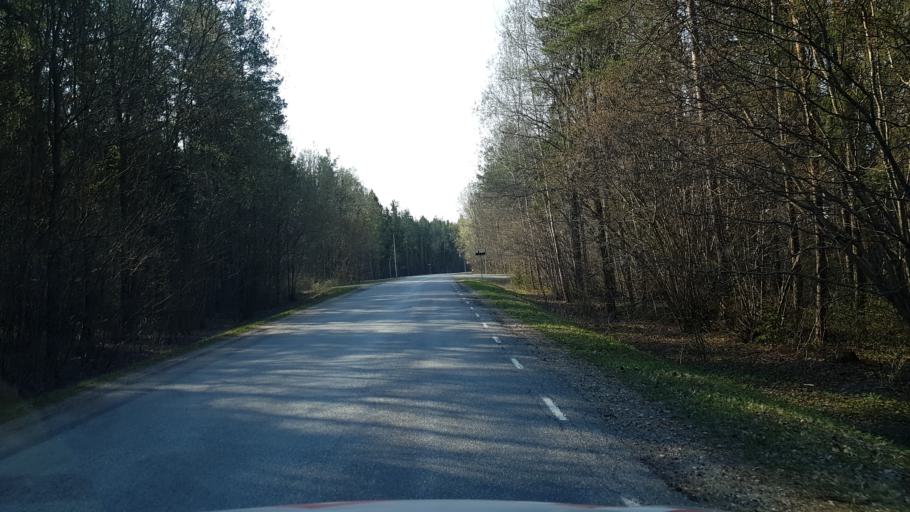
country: EE
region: Raplamaa
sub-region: Kohila vald
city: Kohila
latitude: 59.1763
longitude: 24.6560
